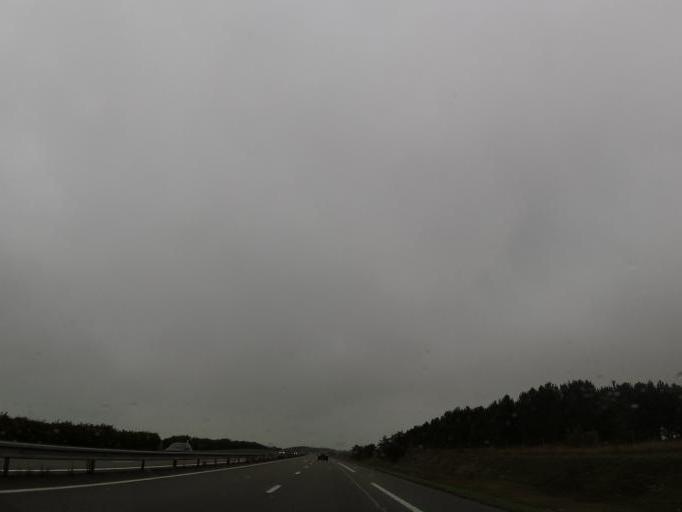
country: FR
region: Champagne-Ardenne
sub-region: Departement de la Marne
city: Chalons-en-Champagne
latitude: 49.0346
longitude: 4.3752
